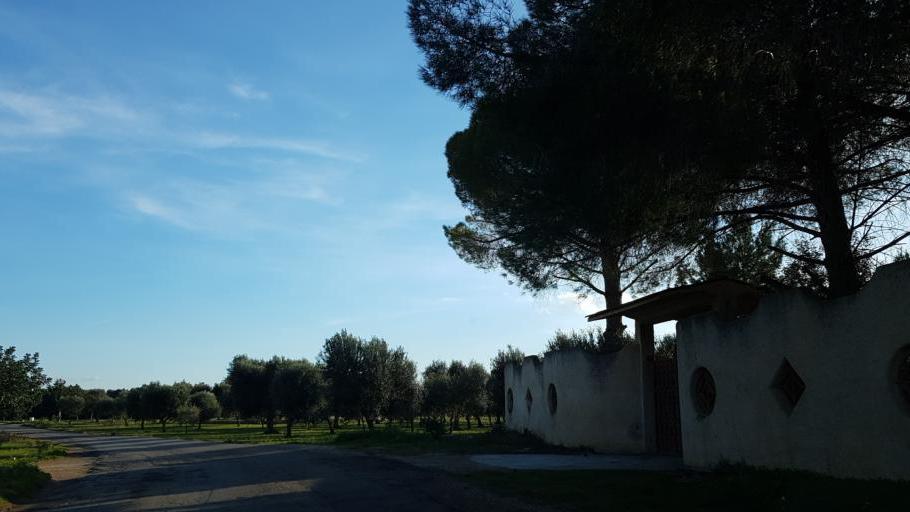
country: IT
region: Apulia
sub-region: Provincia di Brindisi
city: San Vito dei Normanni
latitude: 40.6721
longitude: 17.7770
